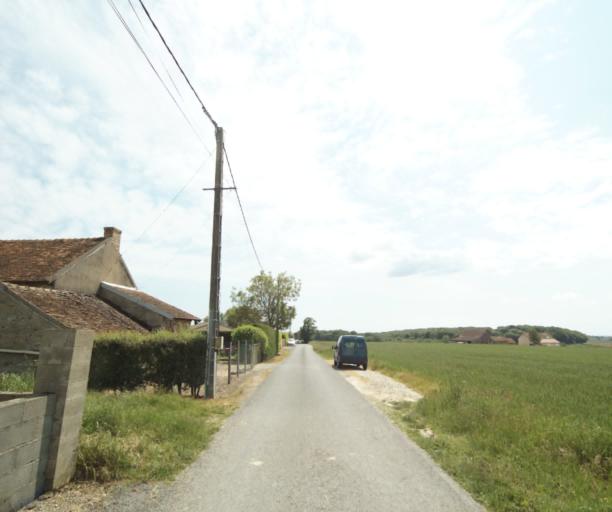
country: FR
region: Bourgogne
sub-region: Departement de Saone-et-Loire
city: Gueugnon
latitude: 46.5965
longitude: 4.1321
